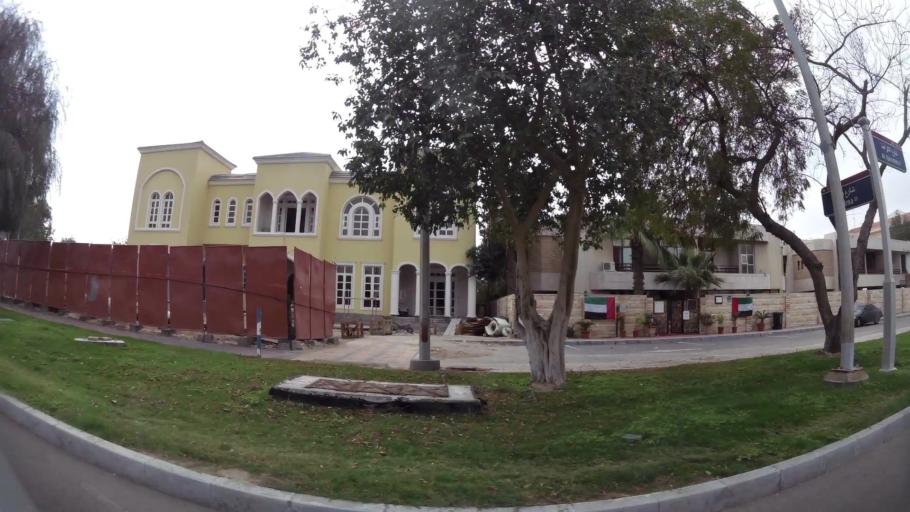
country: AE
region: Abu Dhabi
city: Abu Dhabi
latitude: 24.4593
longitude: 54.3722
